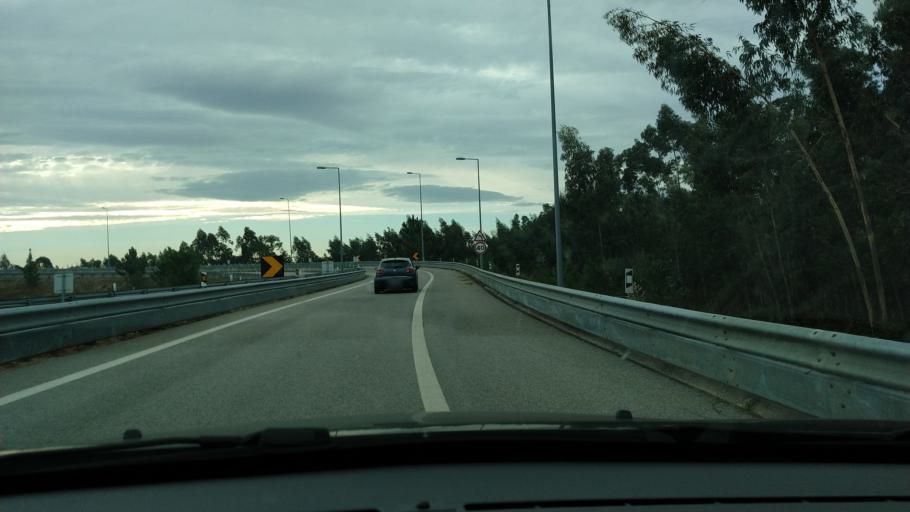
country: PT
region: Coimbra
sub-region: Figueira da Foz
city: Alhadas
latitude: 40.1529
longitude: -8.7843
